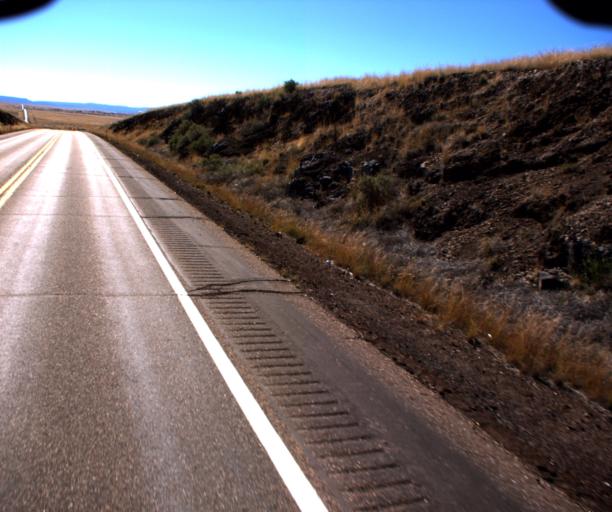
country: US
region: Arizona
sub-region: Apache County
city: Springerville
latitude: 34.2999
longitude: -109.3764
